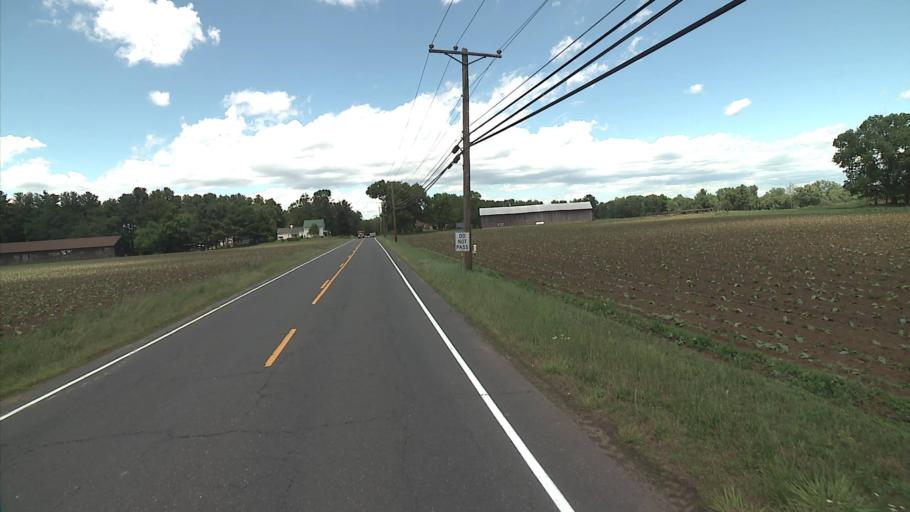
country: US
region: Connecticut
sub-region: Hartford County
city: Hazardville
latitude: 42.0038
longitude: -72.5419
